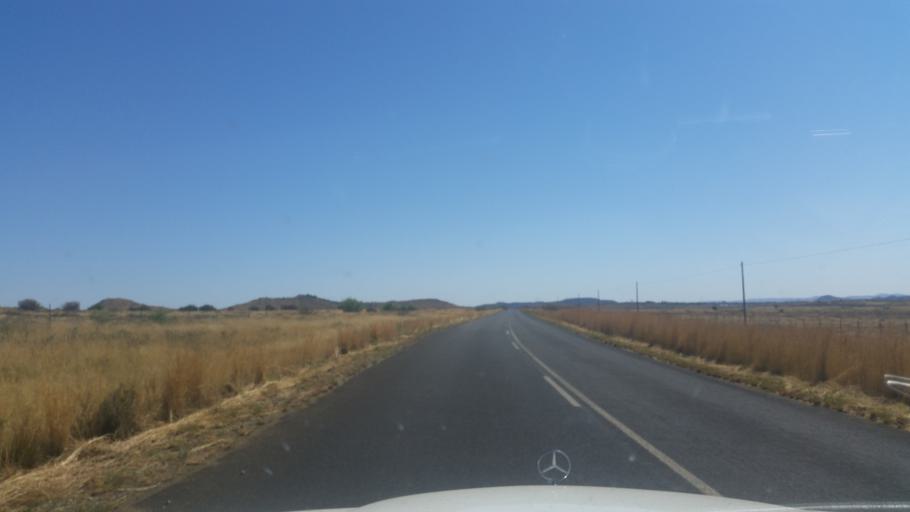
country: ZA
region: Eastern Cape
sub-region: Joe Gqabi District Municipality
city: Burgersdorp
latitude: -30.7383
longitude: 25.7546
